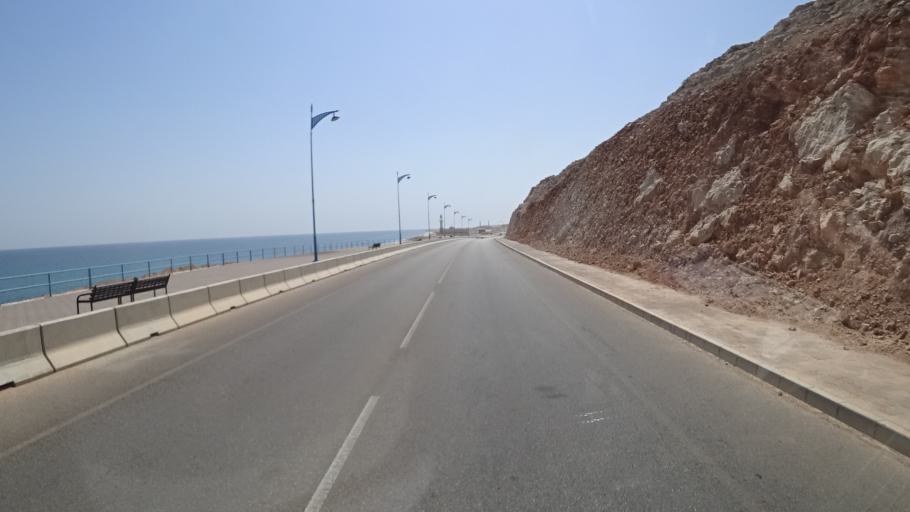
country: OM
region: Ash Sharqiyah
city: Sur
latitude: 22.5661
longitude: 59.5701
